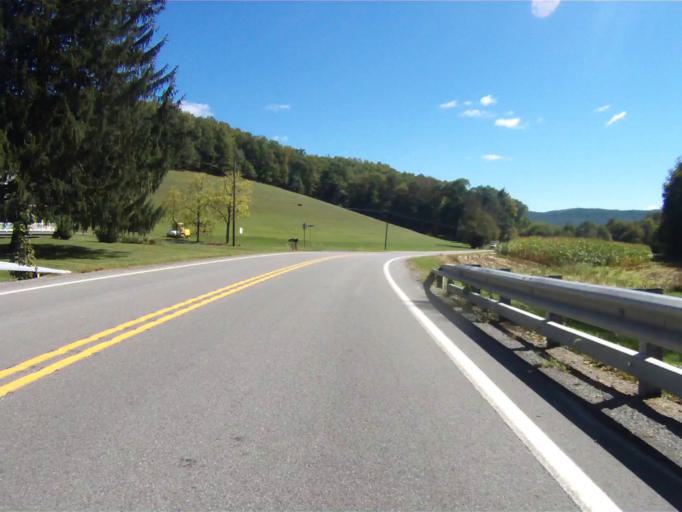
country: US
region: Pennsylvania
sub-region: Centre County
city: Milesburg
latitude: 40.9233
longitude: -77.8997
